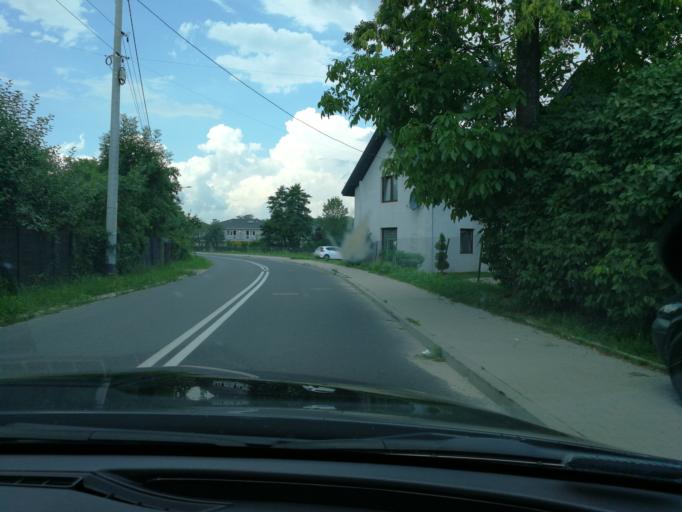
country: PL
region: Lodz Voivodeship
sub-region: Skierniewice
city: Skierniewice
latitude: 51.9731
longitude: 20.1275
